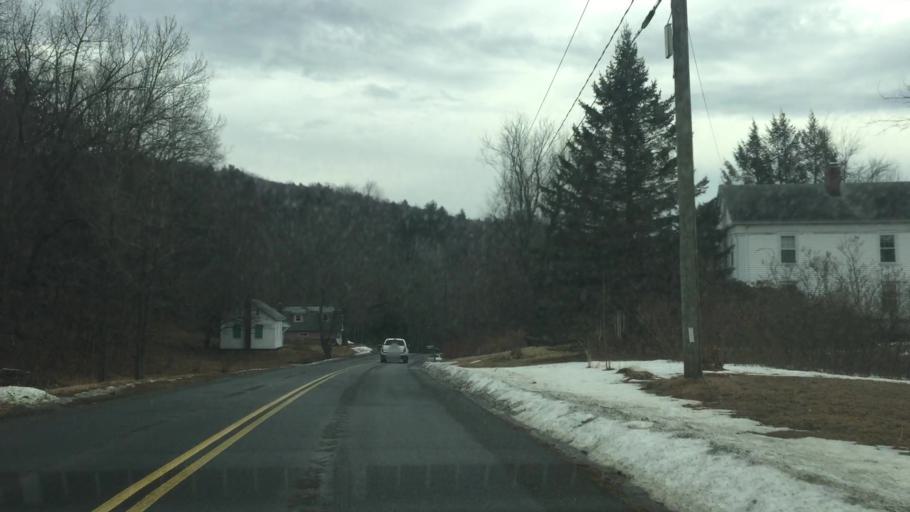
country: US
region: Massachusetts
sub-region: Hampshire County
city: Westhampton
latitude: 42.2145
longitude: -72.8502
